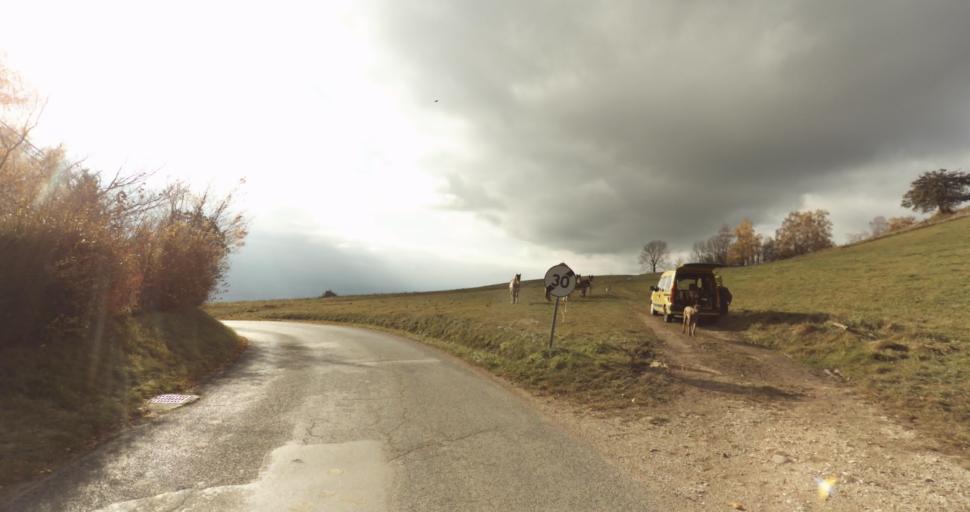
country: FR
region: Rhone-Alpes
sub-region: Departement de la Haute-Savoie
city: Epagny
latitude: 45.9630
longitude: 6.0803
